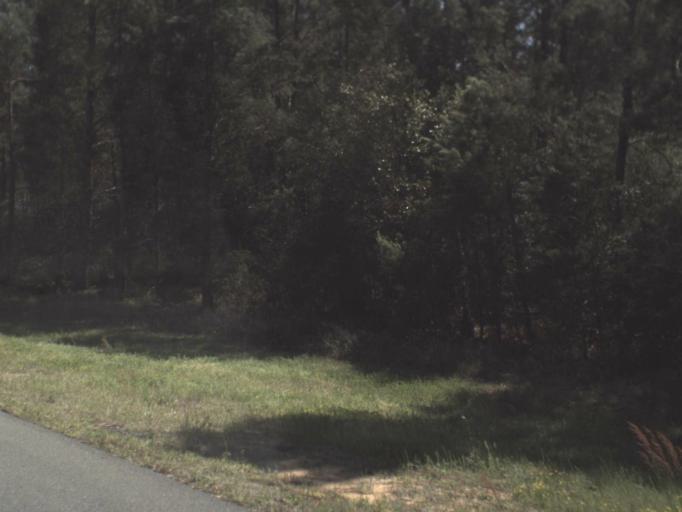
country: US
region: Florida
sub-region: Bay County
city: Youngstown
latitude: 30.4288
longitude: -85.3235
